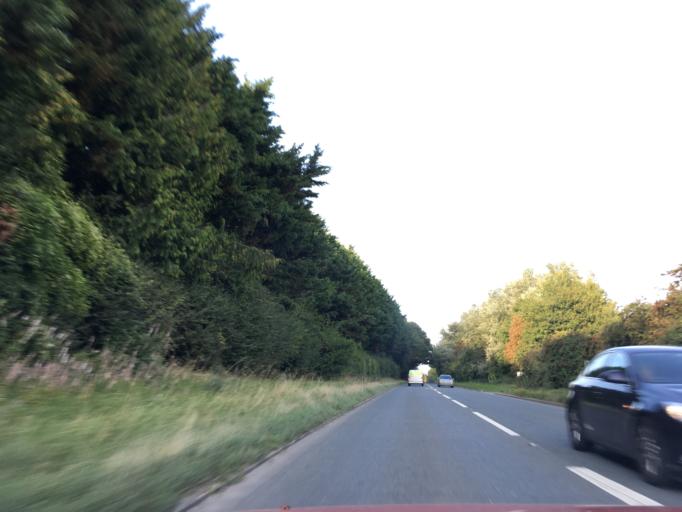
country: GB
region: England
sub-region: Gloucestershire
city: Bourton on the Water
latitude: 51.8884
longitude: -1.7668
